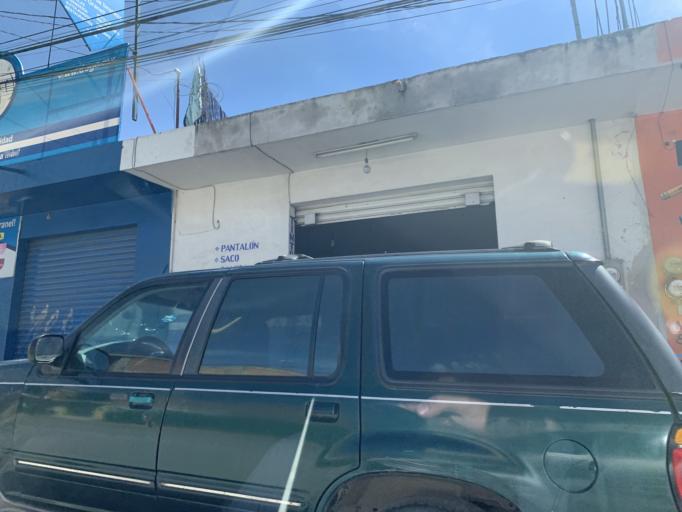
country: MX
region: Puebla
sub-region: Cuautlancingo
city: La Trinidad Chautenco
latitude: 19.0908
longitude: -98.2677
